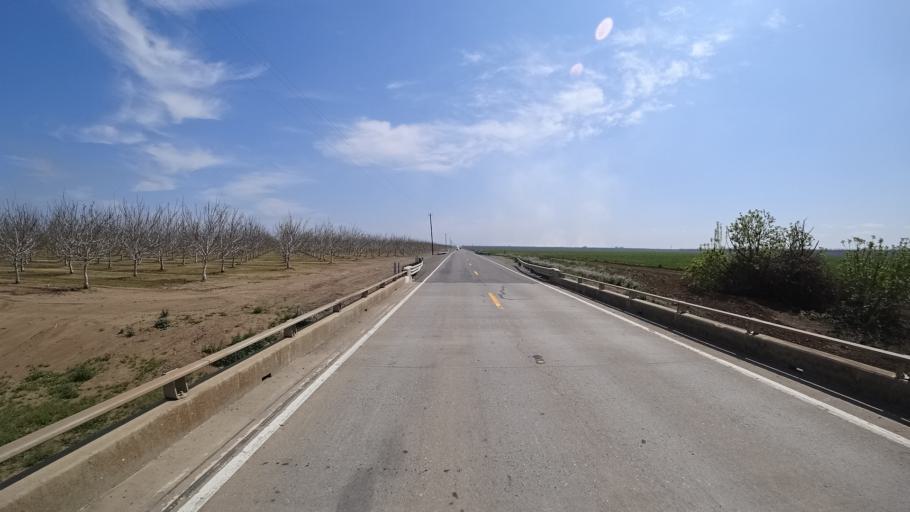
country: US
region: California
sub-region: Butte County
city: Durham
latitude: 39.4643
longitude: -121.9562
